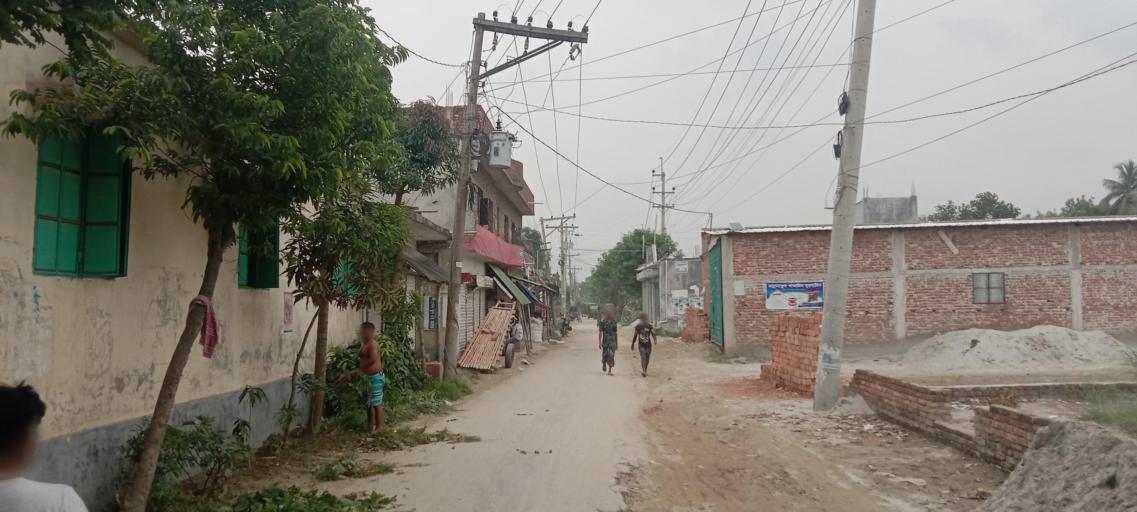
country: BD
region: Dhaka
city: Azimpur
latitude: 23.7061
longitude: 90.3499
